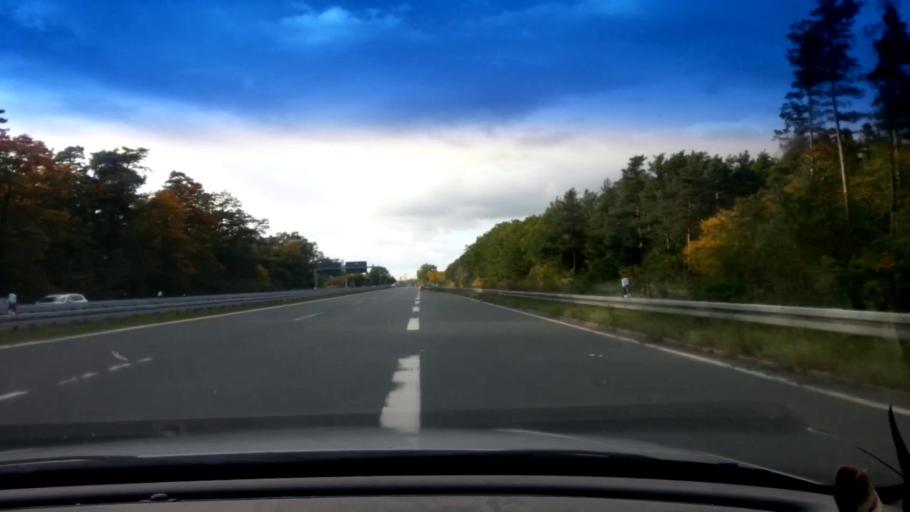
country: DE
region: Bavaria
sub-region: Upper Franconia
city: Bamberg
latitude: 49.8745
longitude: 10.9355
